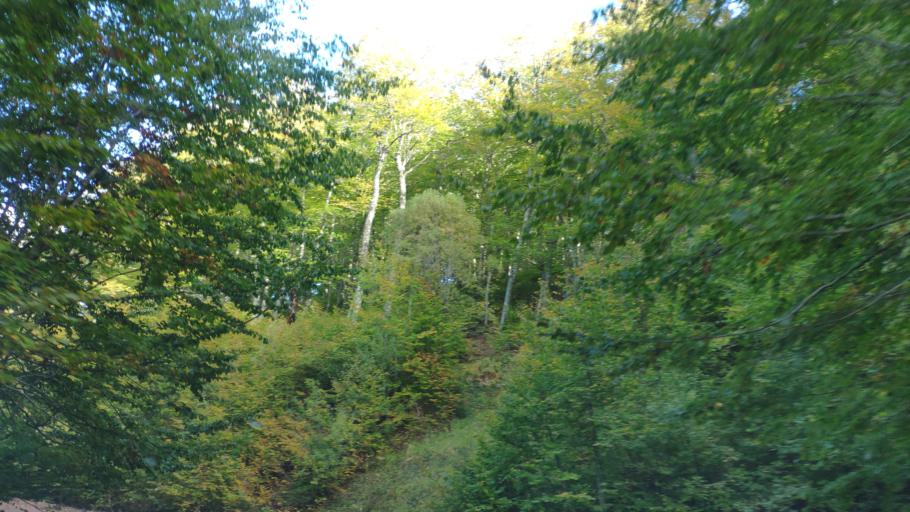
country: GR
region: West Macedonia
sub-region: Nomos Kastorias
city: Nestorio
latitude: 40.3228
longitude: 20.9069
